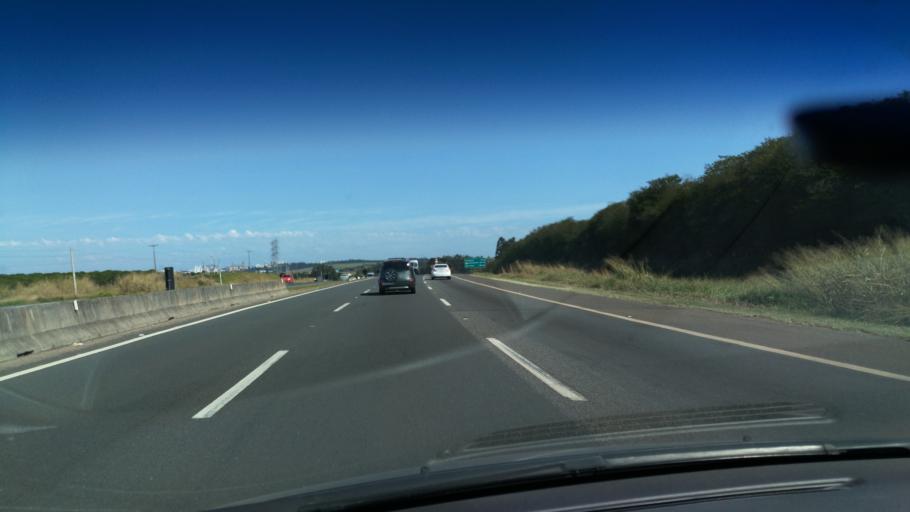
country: BR
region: Sao Paulo
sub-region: Jaguariuna
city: Jaguariuna
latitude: -22.7777
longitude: -47.0236
